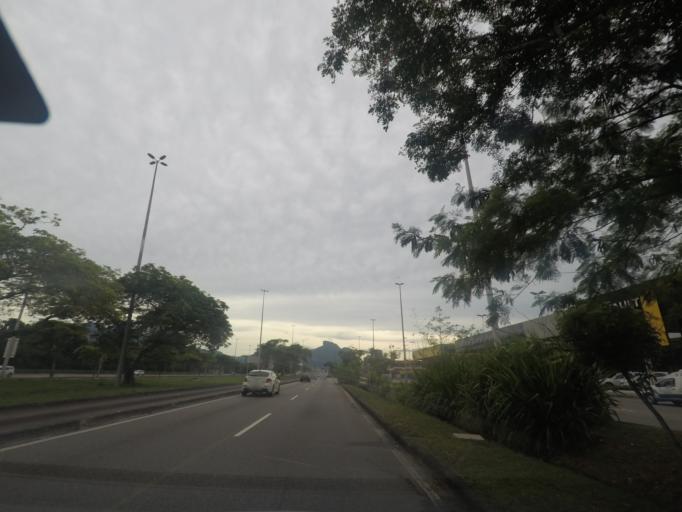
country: BR
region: Rio de Janeiro
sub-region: Rio De Janeiro
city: Rio de Janeiro
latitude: -23.0004
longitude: -43.3738
